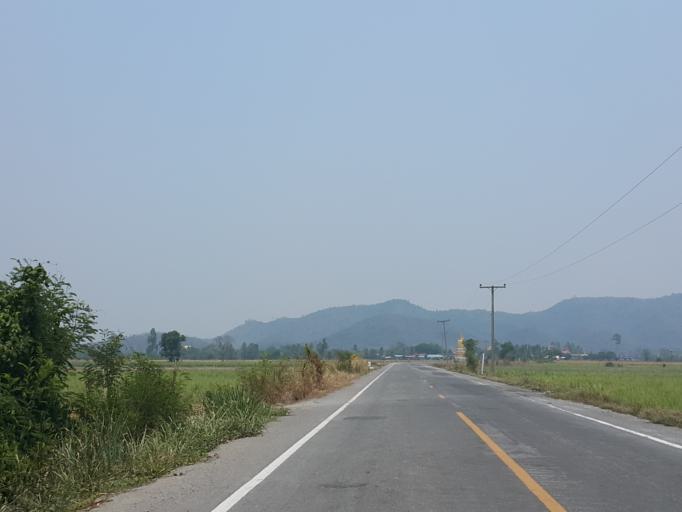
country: TH
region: Kamphaeng Phet
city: Pang Sila Thong
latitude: 16.0556
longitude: 99.3675
